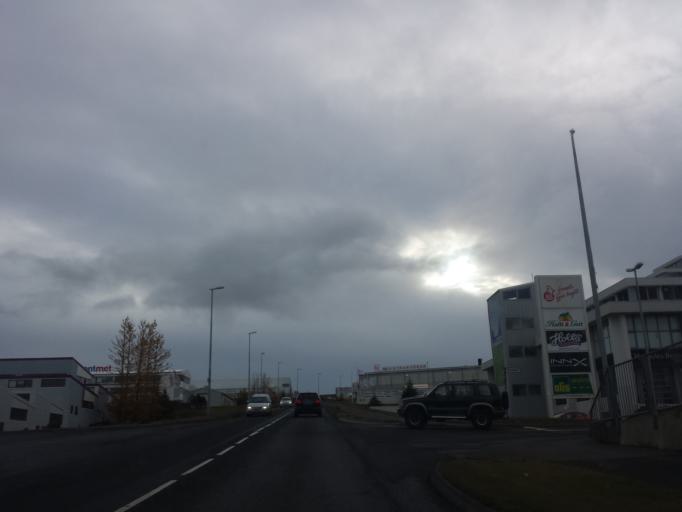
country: IS
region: Capital Region
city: Reykjavik
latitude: 64.1228
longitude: -21.7969
